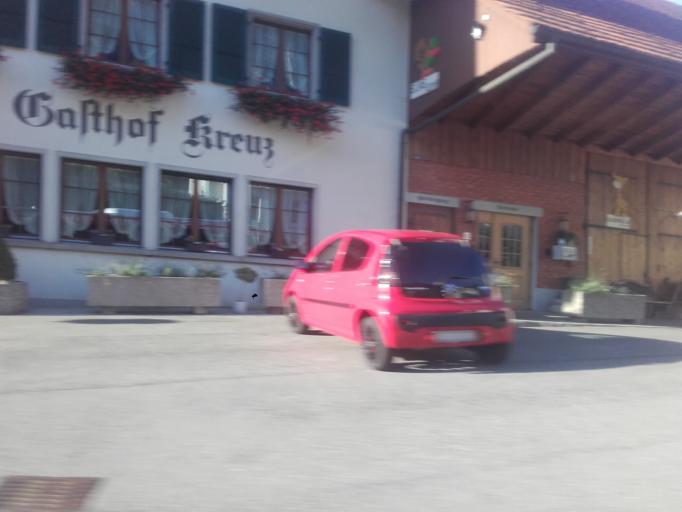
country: CH
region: Solothurn
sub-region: Bezirk Thal
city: Welschenrohr
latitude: 47.2811
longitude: 7.5299
